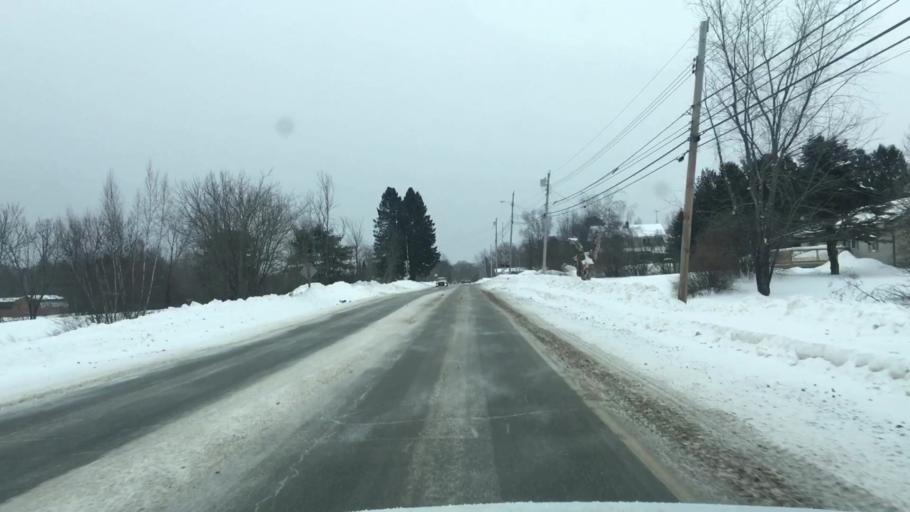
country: US
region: Maine
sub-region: Penobscot County
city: Lincoln
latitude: 45.3963
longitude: -68.4926
